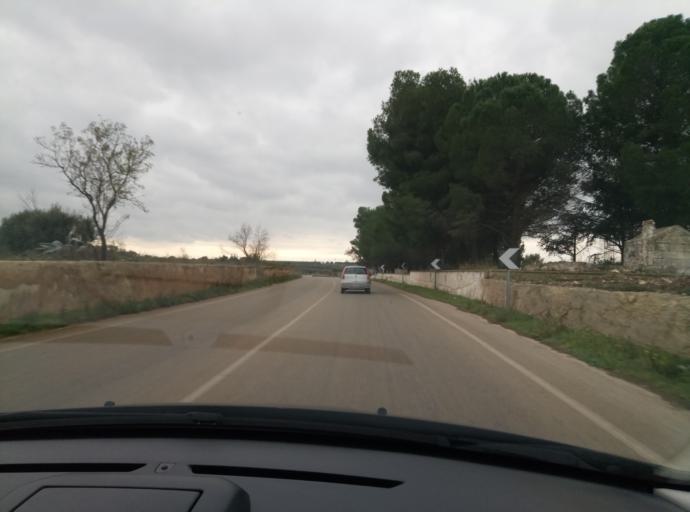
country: IT
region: Apulia
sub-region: Provincia di Bari
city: Adelfia
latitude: 40.9594
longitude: 16.8651
